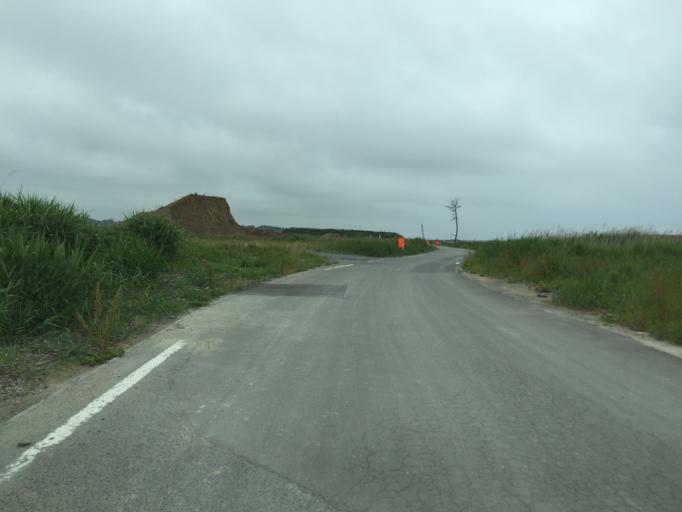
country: JP
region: Fukushima
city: Namie
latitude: 37.6893
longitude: 141.0093
